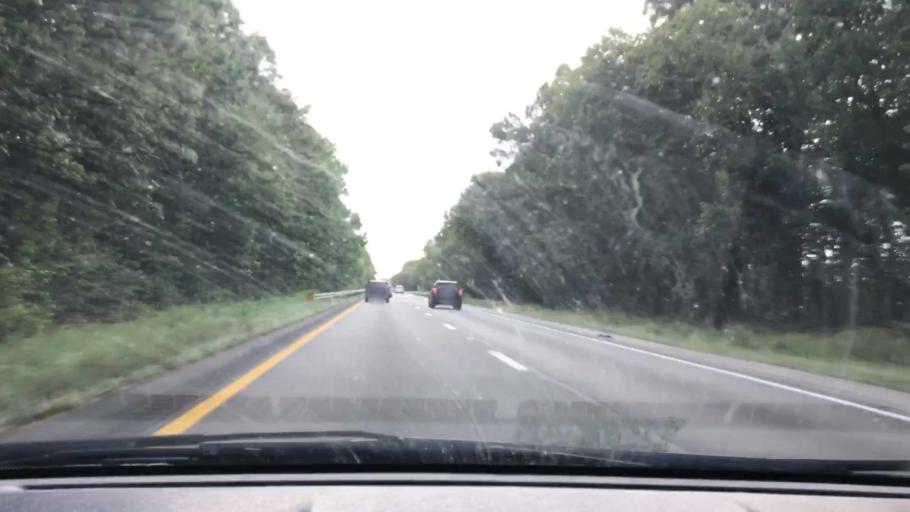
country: US
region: Virginia
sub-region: Henrico County
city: Wyndham
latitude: 37.6976
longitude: -77.7279
